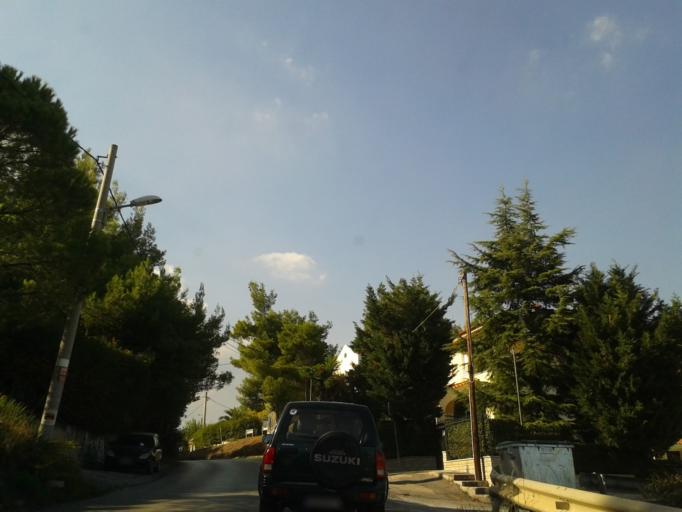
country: GR
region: Attica
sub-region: Nomarchia Anatolikis Attikis
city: Anoixi
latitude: 38.1374
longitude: 23.8703
